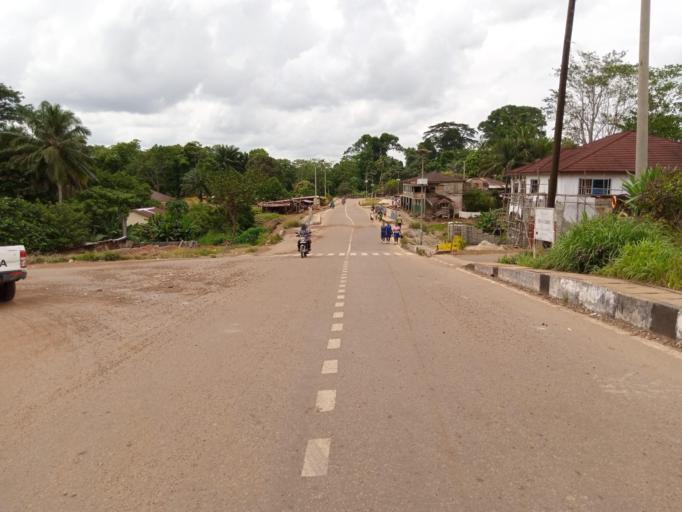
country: SL
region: Southern Province
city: Moyamba
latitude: 8.1593
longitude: -12.4304
